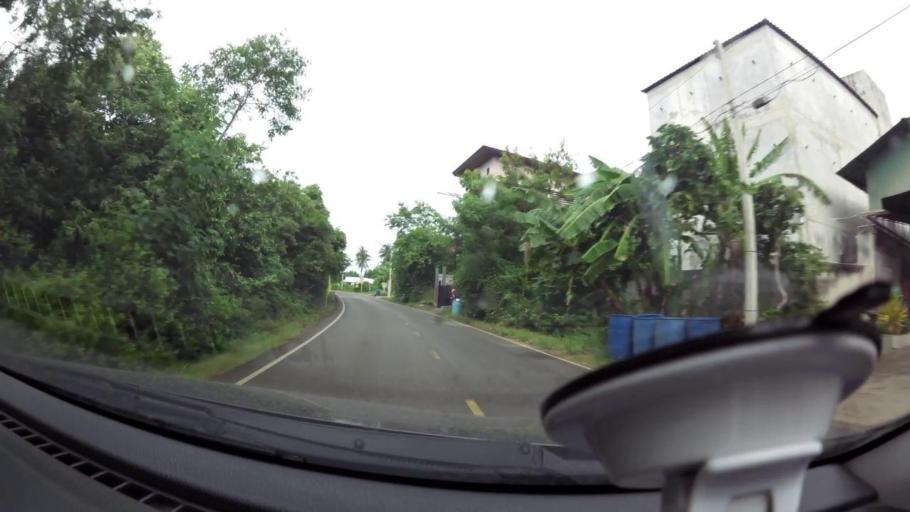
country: TH
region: Prachuap Khiri Khan
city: Pran Buri
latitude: 12.3912
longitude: 99.9816
